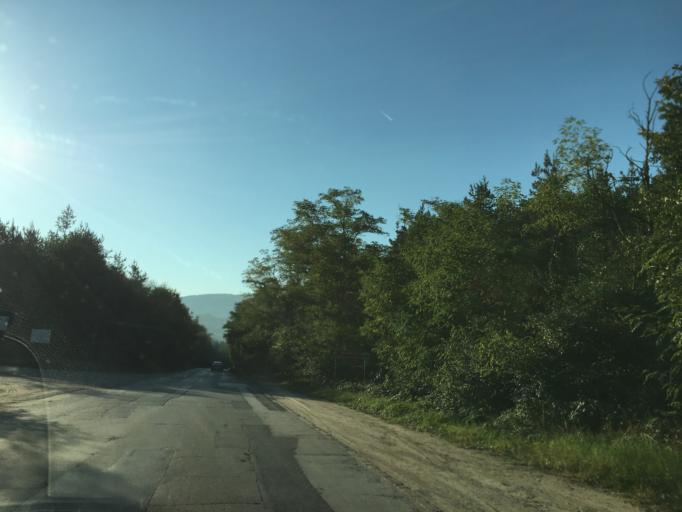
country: BG
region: Sofiya
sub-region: Obshtina Ikhtiman
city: Ikhtiman
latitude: 42.3732
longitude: 23.8803
